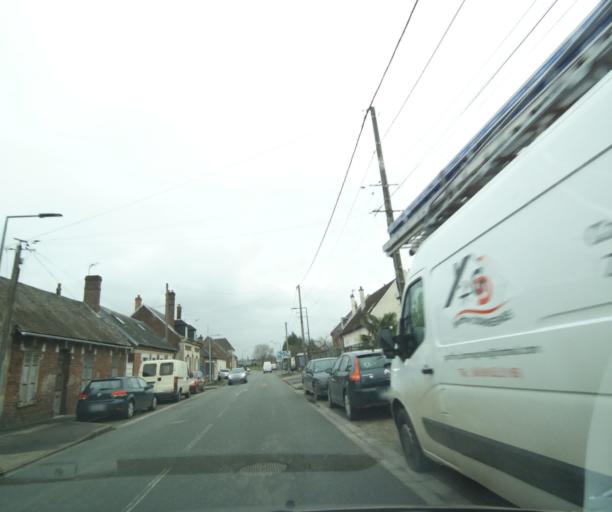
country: FR
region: Picardie
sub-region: Departement de l'Oise
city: Noyon
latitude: 49.5710
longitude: 3.0180
